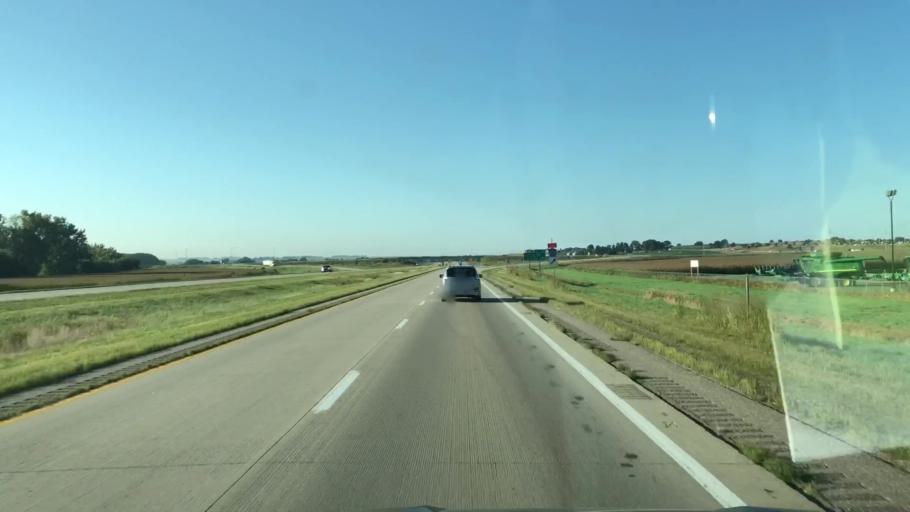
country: US
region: Iowa
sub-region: Plymouth County
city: Le Mars
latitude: 42.7709
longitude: -96.2095
